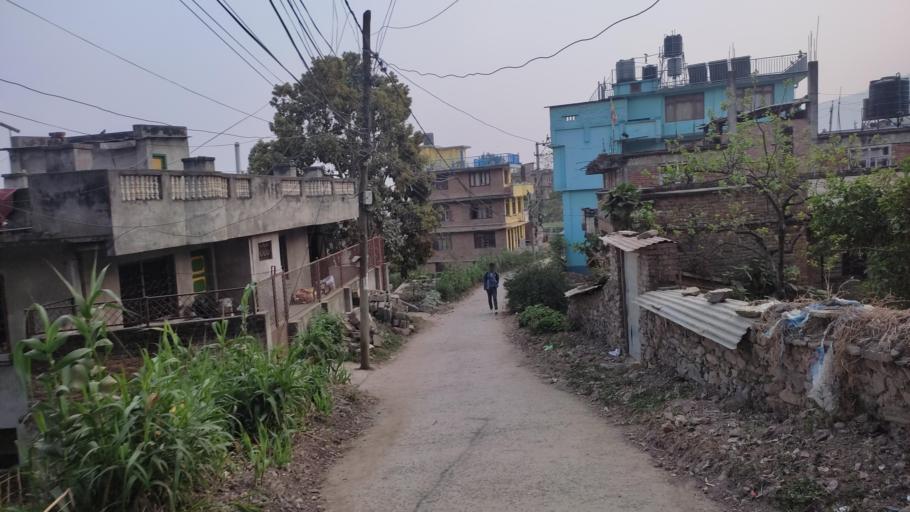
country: NP
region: Central Region
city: Kirtipur
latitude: 27.6683
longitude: 85.2767
